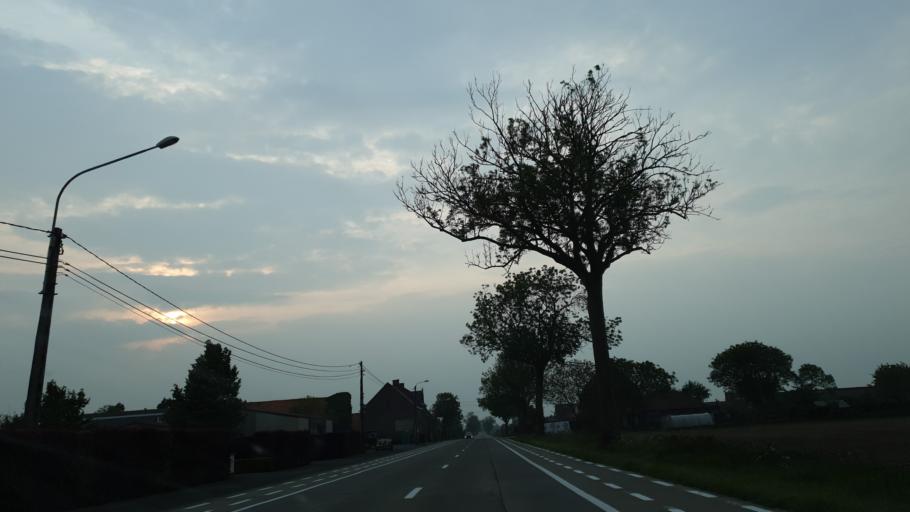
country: BE
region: Flanders
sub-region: Provincie West-Vlaanderen
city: Poperinge
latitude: 50.9172
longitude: 2.7617
